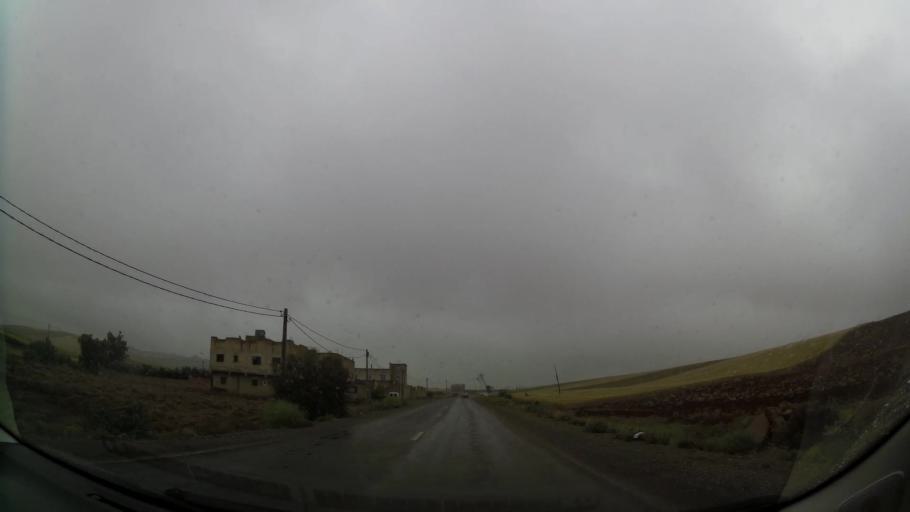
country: MA
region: Oriental
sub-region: Nador
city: Boudinar
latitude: 35.1395
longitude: -3.6188
